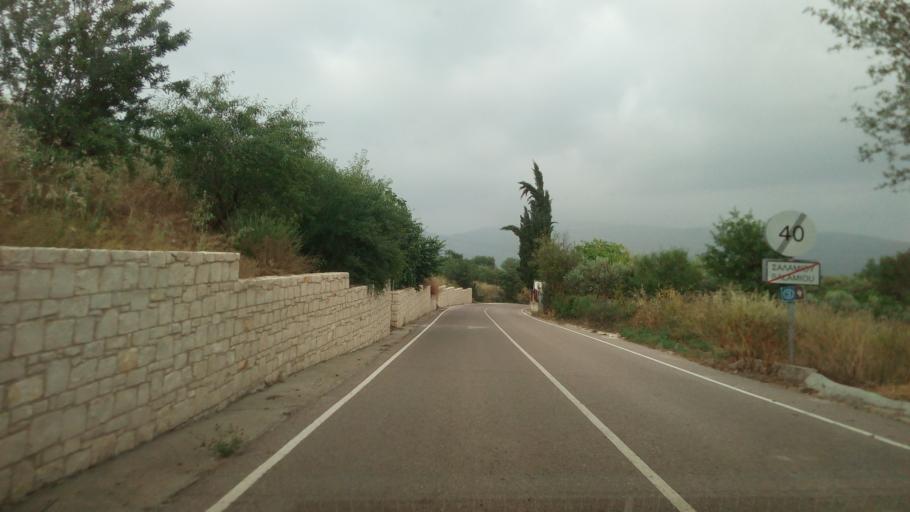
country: CY
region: Limassol
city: Pachna
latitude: 34.8418
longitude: 32.6929
